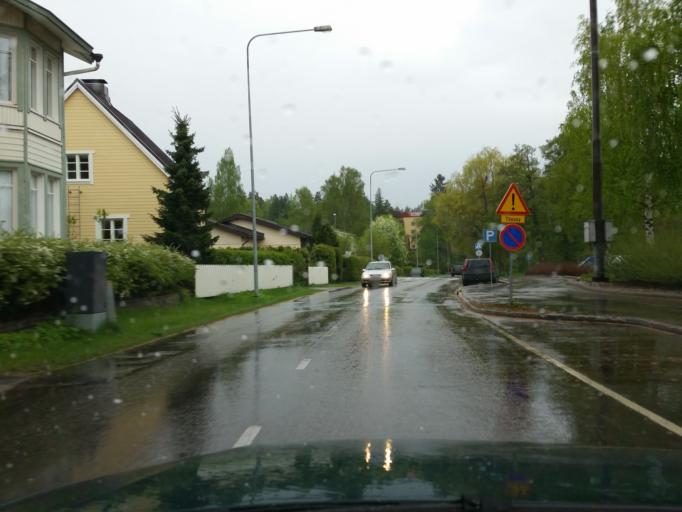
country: FI
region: Uusimaa
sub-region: Helsinki
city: Lohja
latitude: 60.2491
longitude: 24.0554
